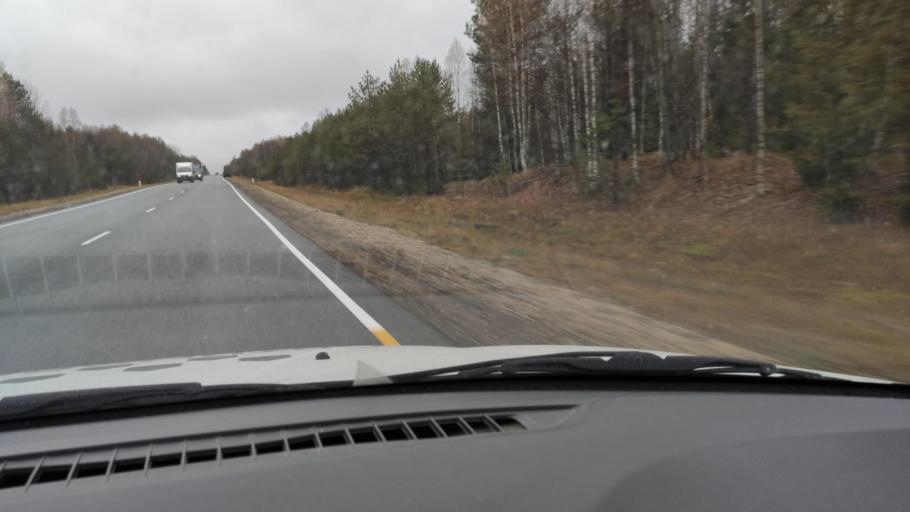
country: RU
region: Kirov
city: Chernaya Kholunitsa
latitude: 58.8072
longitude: 51.8451
